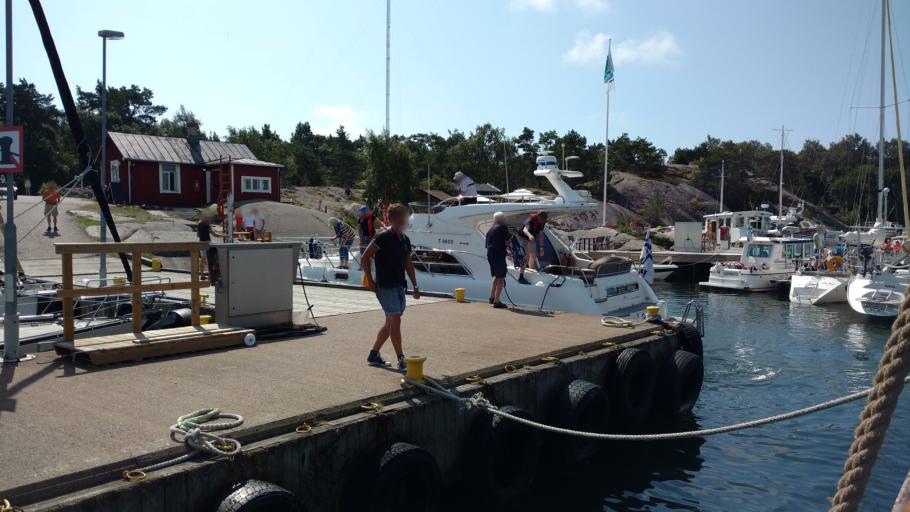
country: FI
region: Varsinais-Suomi
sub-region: Aboland-Turunmaa
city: Dragsfjaerd
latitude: 59.8110
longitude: 22.3367
